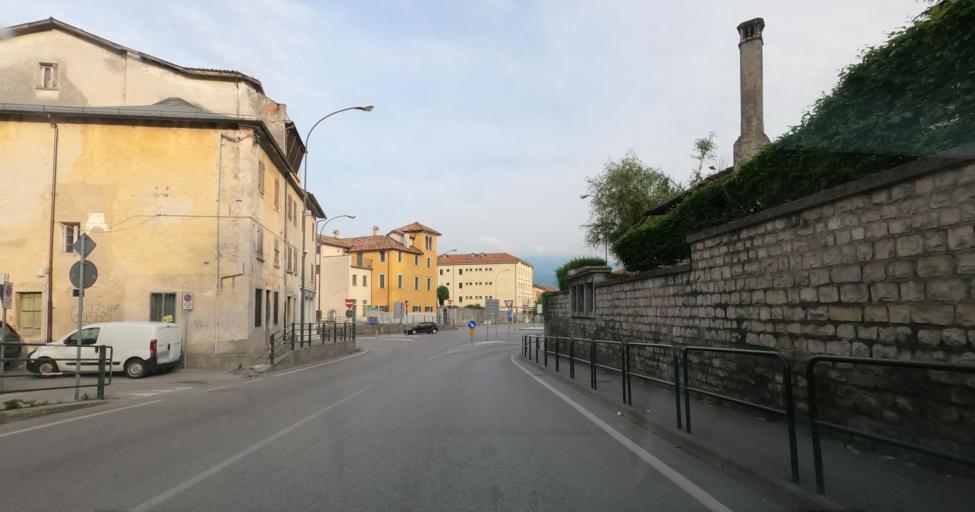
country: IT
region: Veneto
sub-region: Provincia di Belluno
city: Belluno
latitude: 46.1443
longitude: 12.2127
